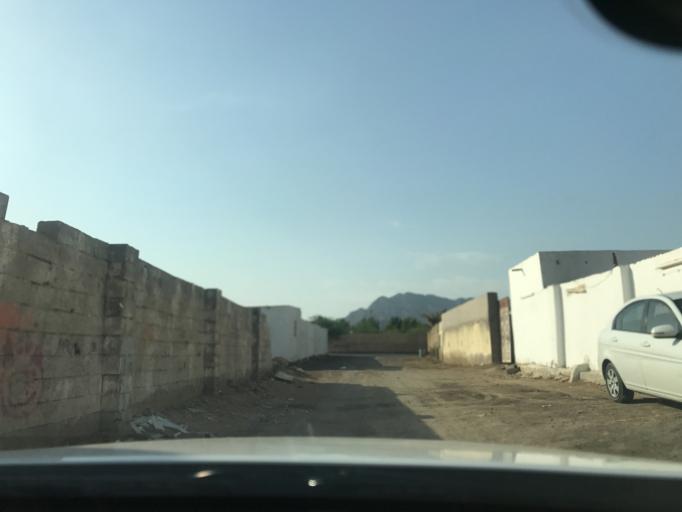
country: SA
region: Makkah
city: Al Jumum
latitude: 21.4377
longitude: 39.5196
